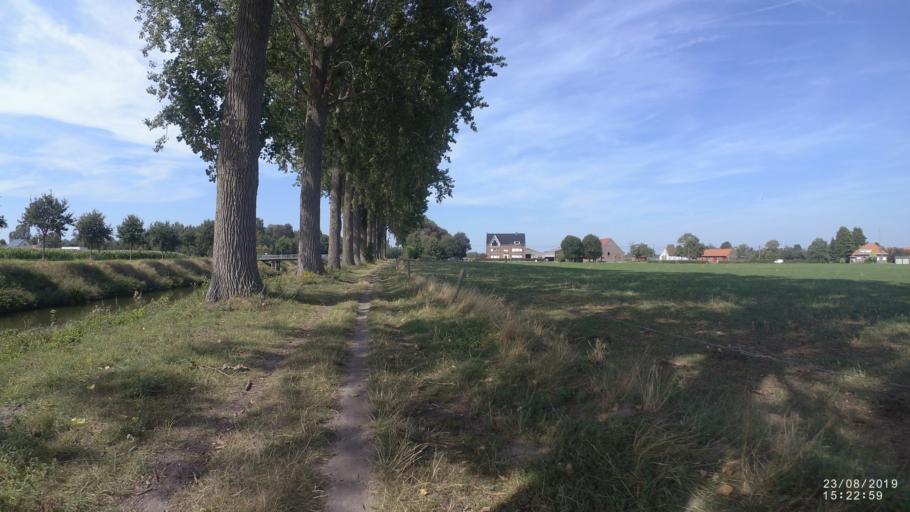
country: BE
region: Flanders
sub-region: Provincie Oost-Vlaanderen
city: Zomergem
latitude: 51.1279
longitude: 3.5649
